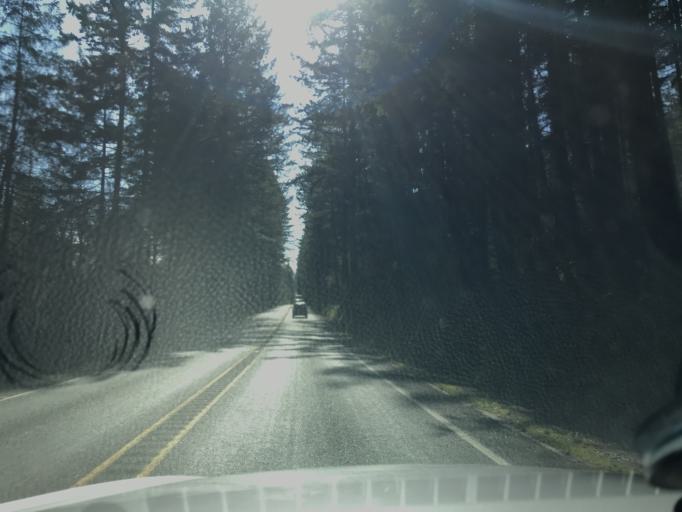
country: US
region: Washington
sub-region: Pierce County
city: Key Center
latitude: 47.3599
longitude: -122.7297
